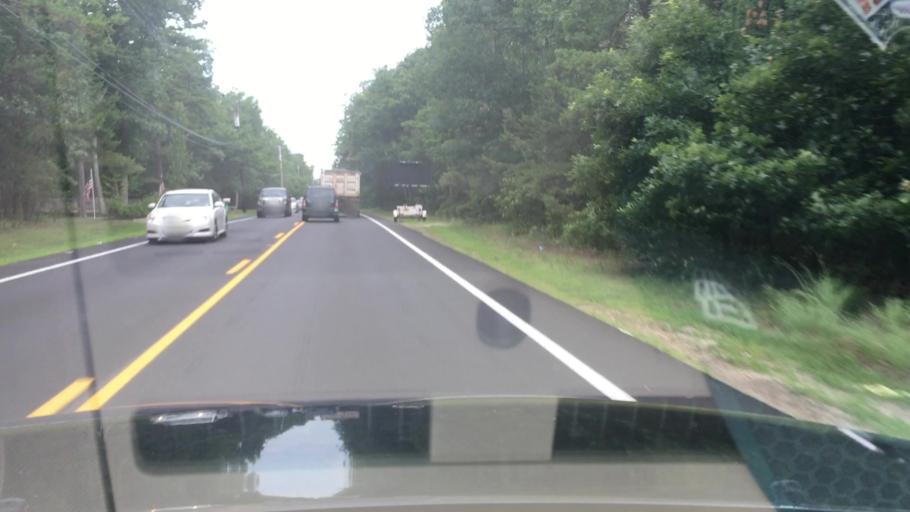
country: US
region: New Jersey
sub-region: Ocean County
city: Lakehurst
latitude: 40.0516
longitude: -74.3375
